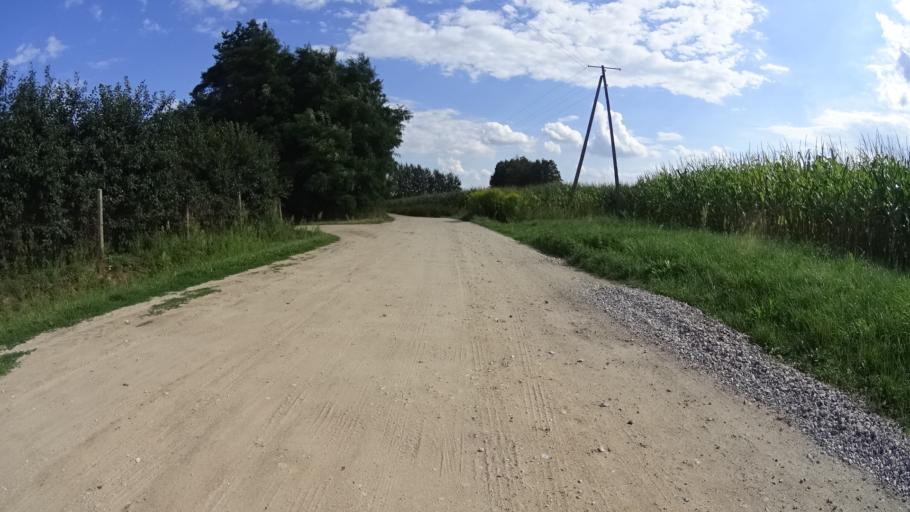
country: PL
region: Masovian Voivodeship
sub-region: Powiat grojecki
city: Mogielnica
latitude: 51.6784
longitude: 20.7655
